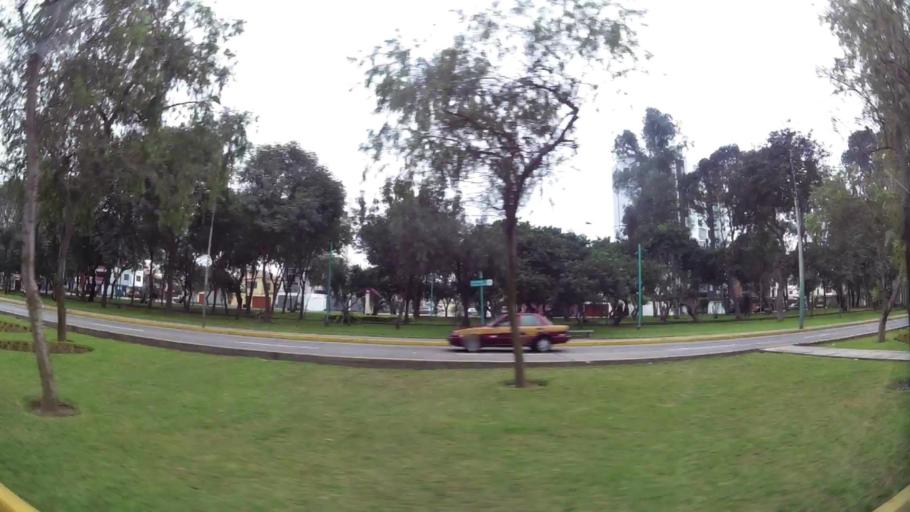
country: PE
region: Lima
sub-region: Lima
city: San Luis
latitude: -12.1005
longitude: -76.9961
